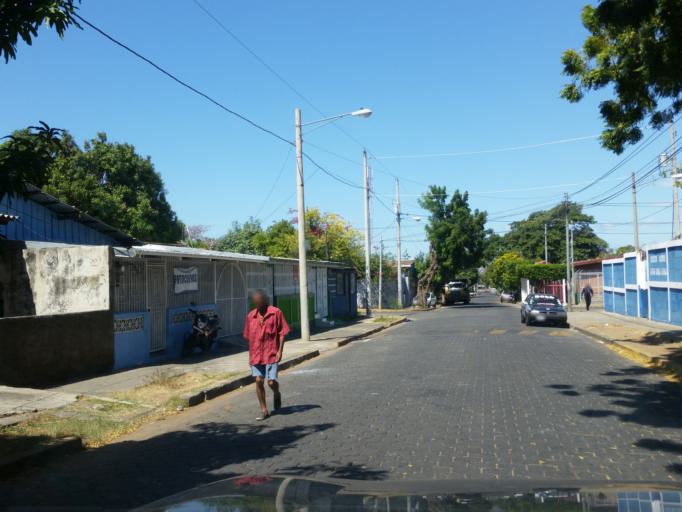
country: NI
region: Managua
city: Ciudad Sandino
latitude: 12.1549
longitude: -86.2998
